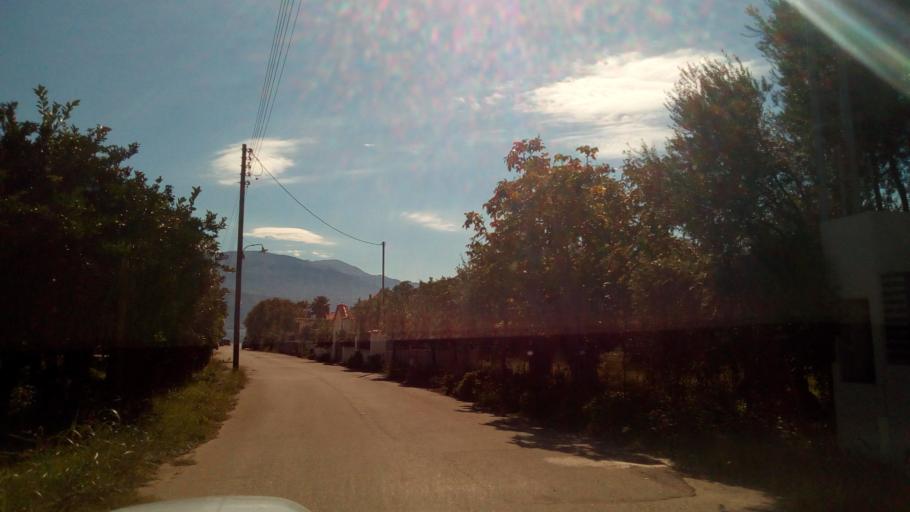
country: GR
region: West Greece
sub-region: Nomos Aitolias kai Akarnanias
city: Nafpaktos
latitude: 38.3782
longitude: 21.8022
